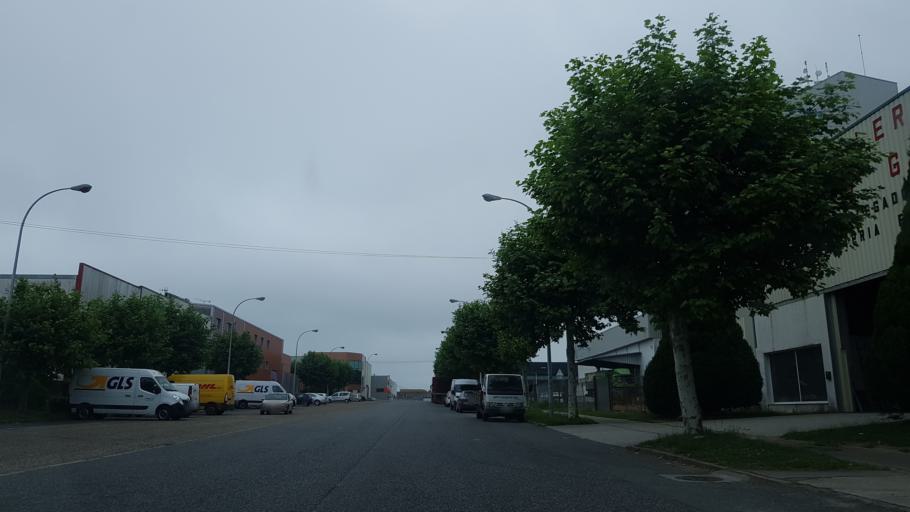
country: ES
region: Galicia
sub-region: Provincia de Lugo
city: Lugo
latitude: 43.0473
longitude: -7.5611
